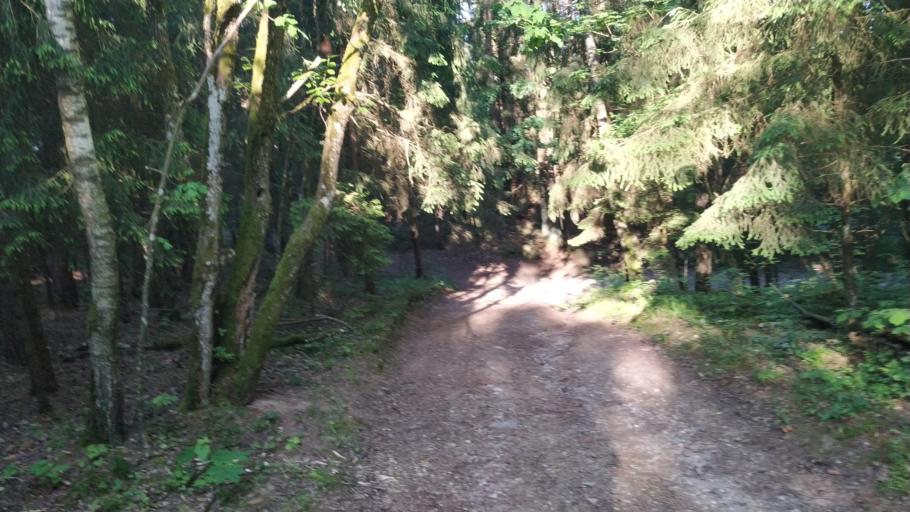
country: LT
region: Utenos apskritis
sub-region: Anyksciai
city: Anyksciai
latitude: 55.5092
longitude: 25.0713
